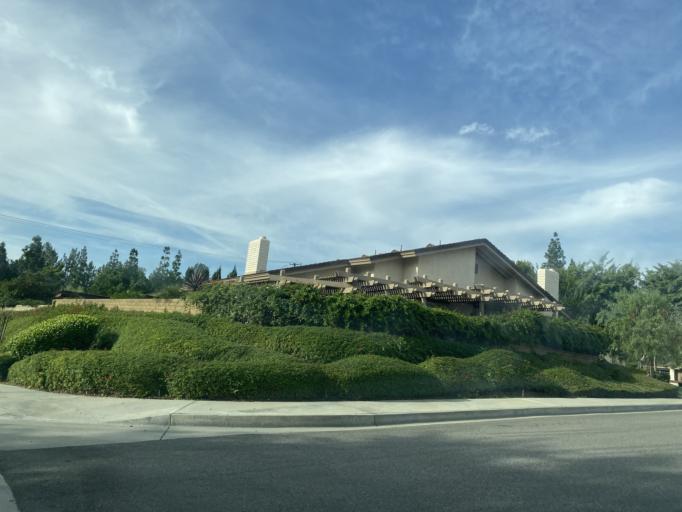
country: US
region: California
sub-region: Orange County
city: Brea
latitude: 33.8952
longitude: -117.8908
